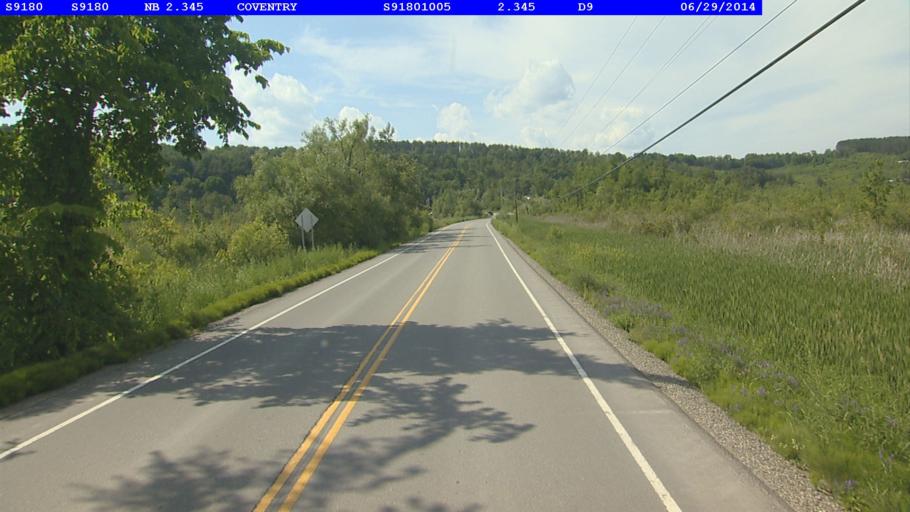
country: US
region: Vermont
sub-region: Orleans County
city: Newport
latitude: 44.9200
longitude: -72.2263
